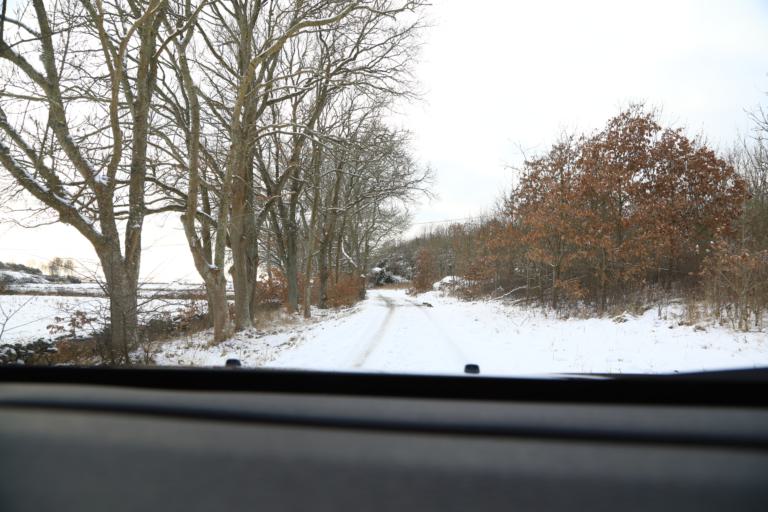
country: SE
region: Halland
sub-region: Kungsbacka Kommun
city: Frillesas
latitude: 57.2173
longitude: 12.1768
